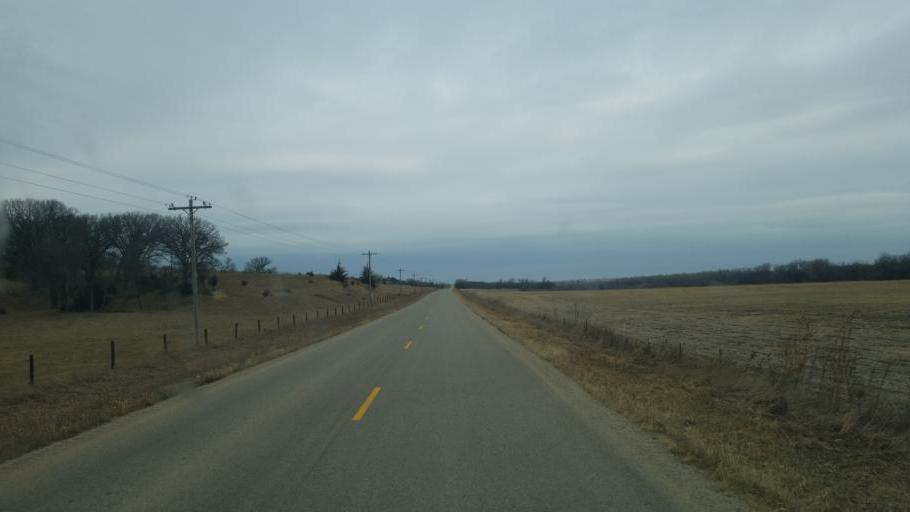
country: US
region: Nebraska
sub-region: Knox County
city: Center
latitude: 42.6442
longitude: -97.8871
